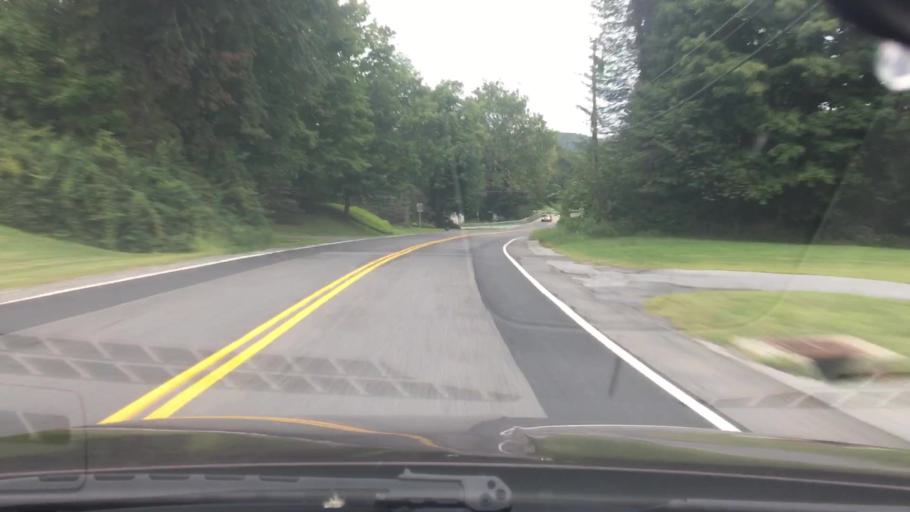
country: US
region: New York
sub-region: Dutchess County
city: Millbrook
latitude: 41.7942
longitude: -73.7026
